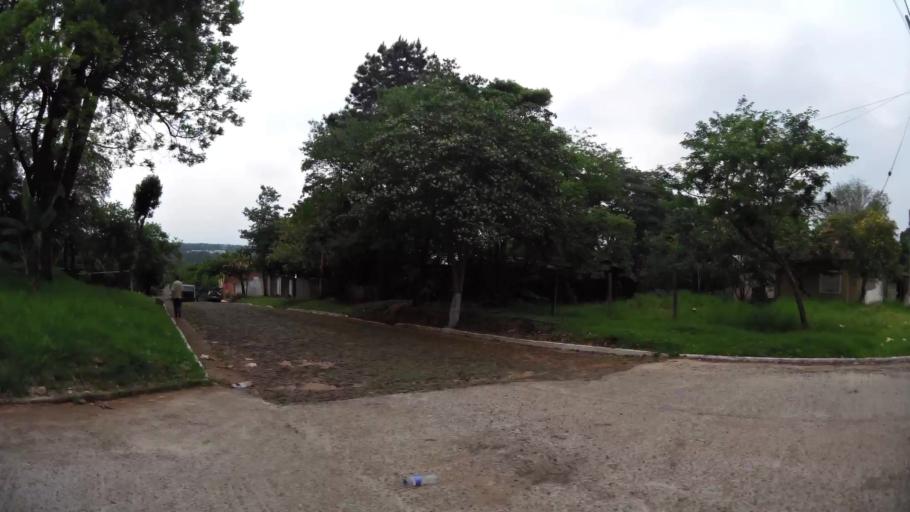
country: BR
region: Parana
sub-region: Foz Do Iguacu
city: Foz do Iguacu
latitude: -25.5603
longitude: -54.6040
